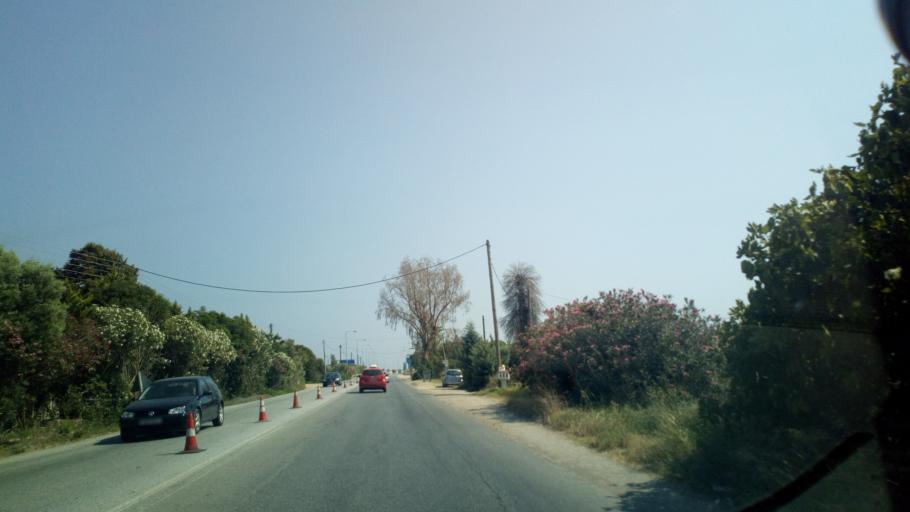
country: GR
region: Central Macedonia
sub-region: Nomos Chalkidikis
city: Nea Potidhaia
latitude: 40.2024
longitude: 23.3259
